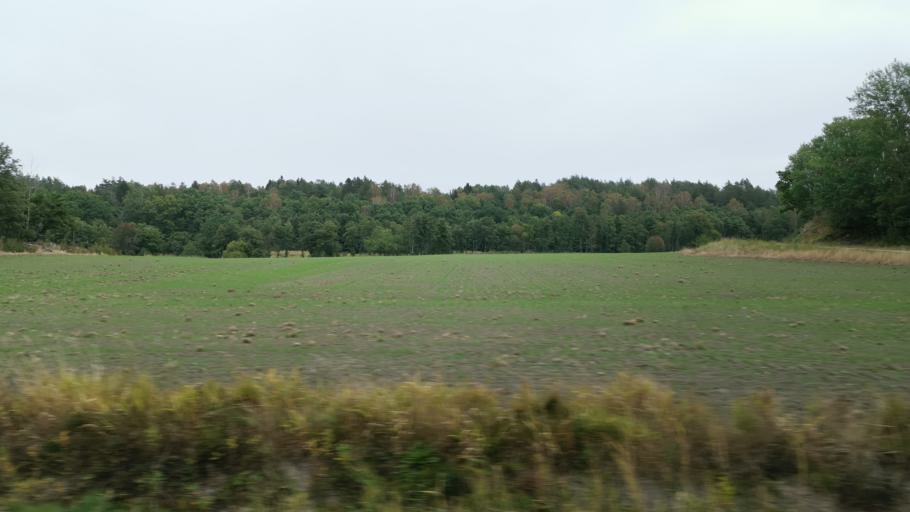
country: SE
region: Vaestra Goetaland
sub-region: Tanums Kommun
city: Tanumshede
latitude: 58.6265
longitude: 11.3511
